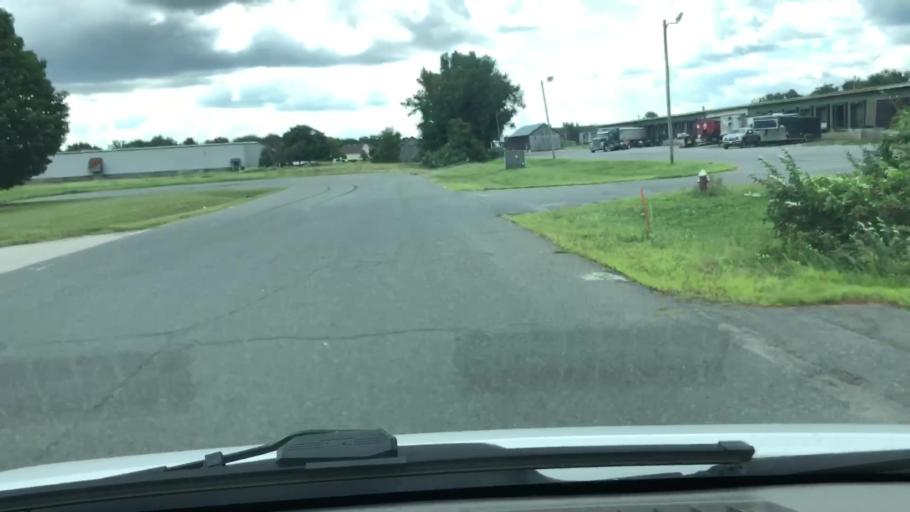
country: US
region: Massachusetts
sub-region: Franklin County
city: South Deerfield
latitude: 42.4659
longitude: -72.6067
